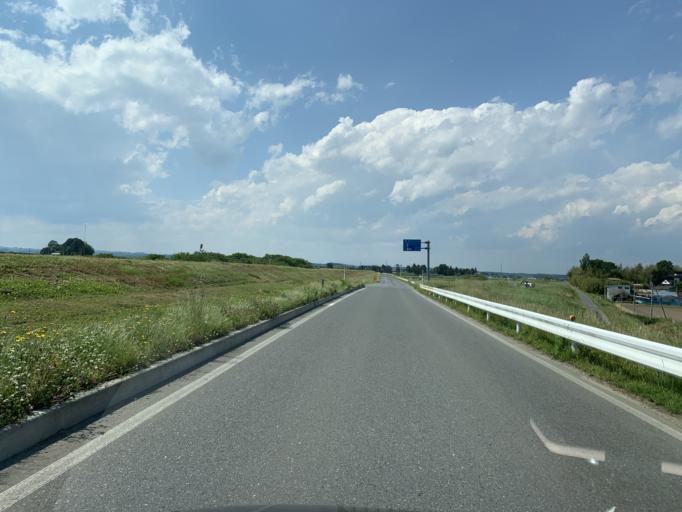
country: JP
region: Miyagi
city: Matsushima
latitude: 38.4378
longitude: 141.1179
